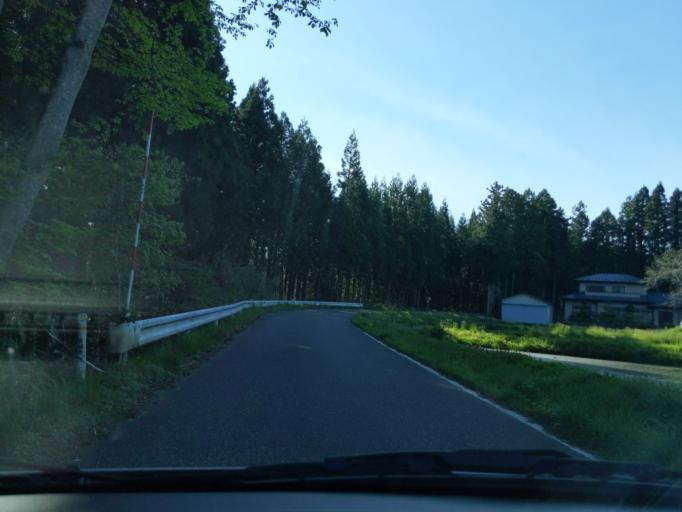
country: JP
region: Iwate
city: Ichinoseki
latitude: 38.8765
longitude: 140.8833
